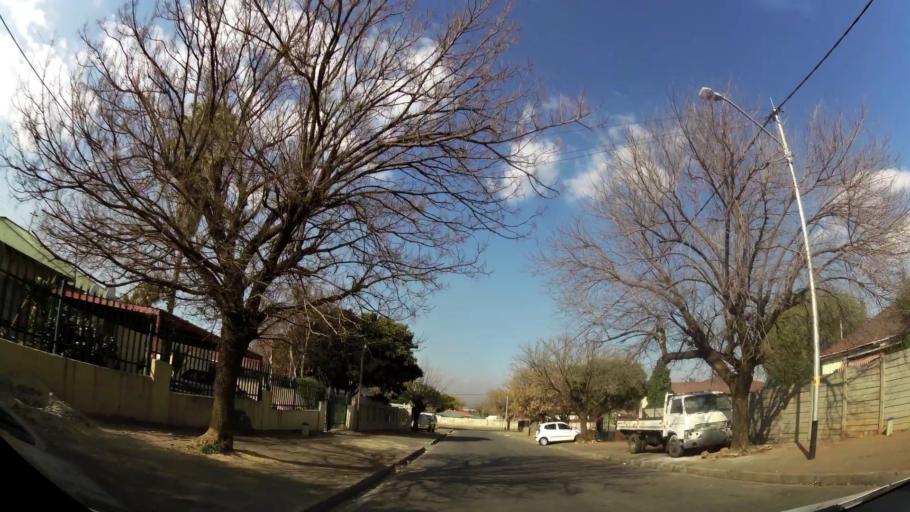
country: ZA
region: Gauteng
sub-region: Ekurhuleni Metropolitan Municipality
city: Germiston
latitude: -26.1794
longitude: 28.1812
